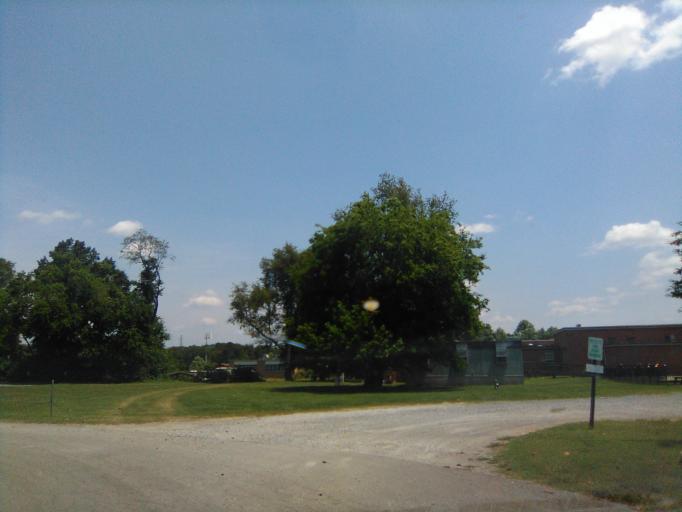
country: US
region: Tennessee
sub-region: Davidson County
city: Belle Meade
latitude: 36.1326
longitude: -86.8436
